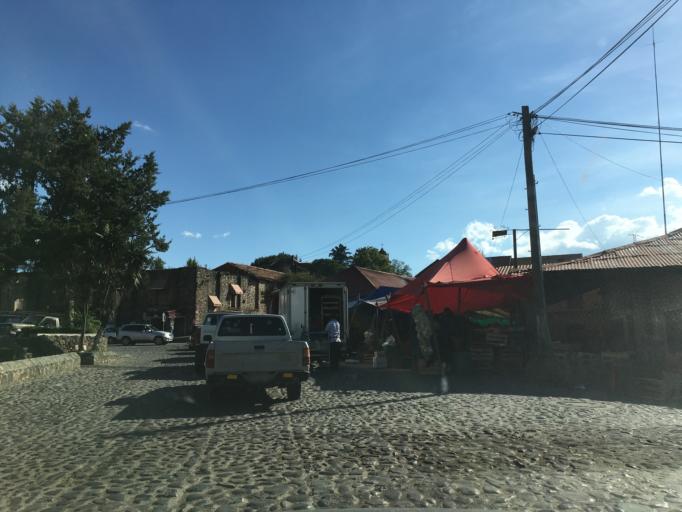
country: MX
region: Hidalgo
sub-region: Omitlan de Juarez
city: San Antonio el Paso
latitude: 20.2043
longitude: -98.5751
